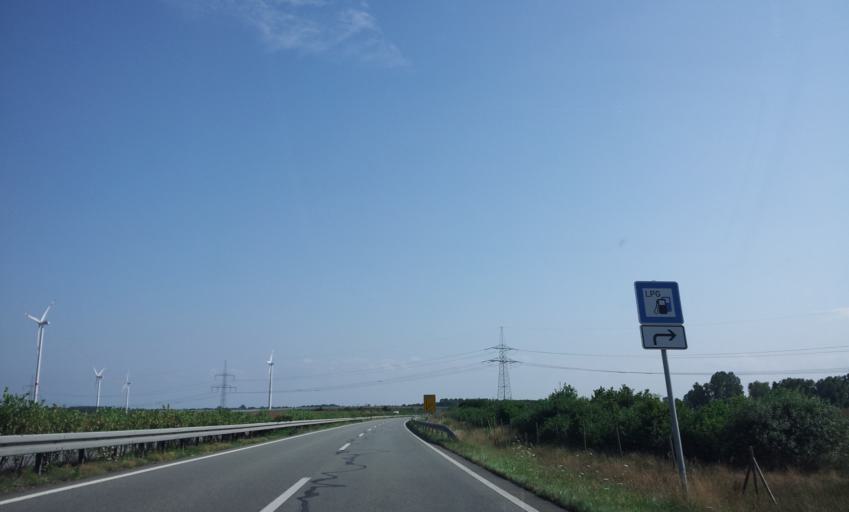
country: DE
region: Mecklenburg-Vorpommern
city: Brandshagen
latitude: 54.1748
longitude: 13.1742
